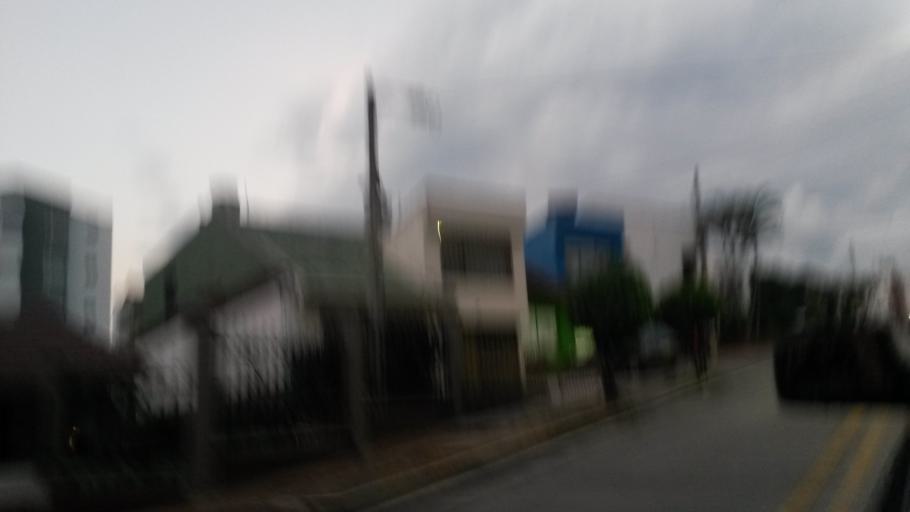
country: CO
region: Quindio
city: Armenia
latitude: 4.5506
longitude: -75.6626
